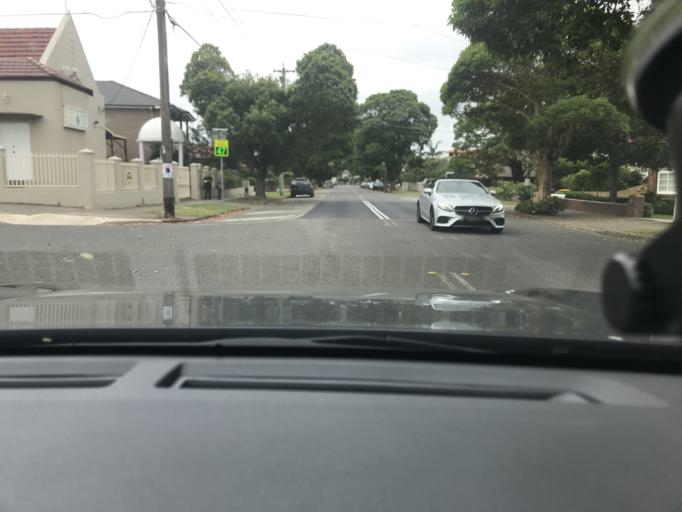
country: AU
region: New South Wales
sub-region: Canada Bay
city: Concord
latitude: -33.8613
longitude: 151.1095
